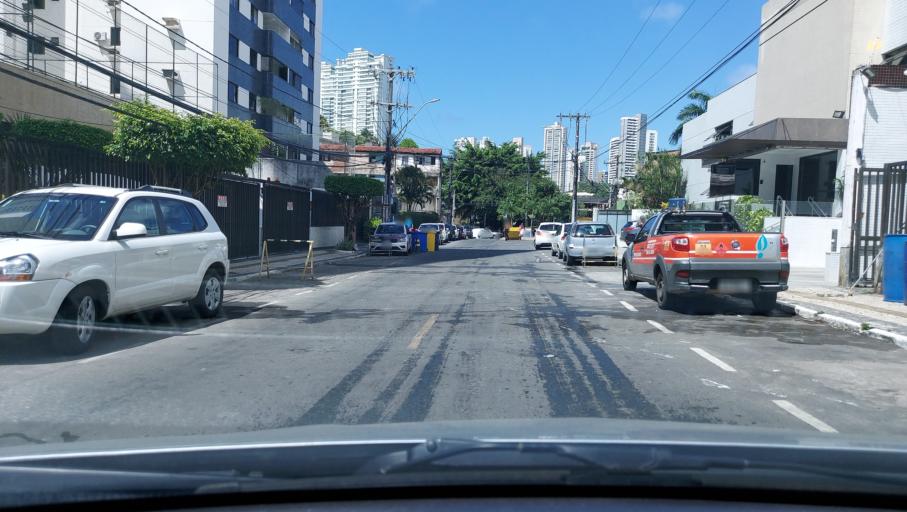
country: BR
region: Bahia
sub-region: Salvador
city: Salvador
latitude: -12.9948
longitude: -38.4795
